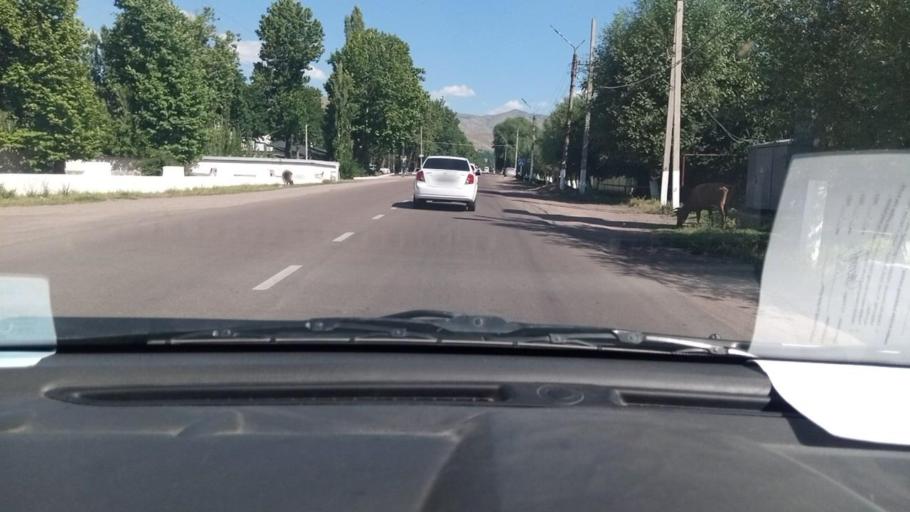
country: UZ
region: Toshkent
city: Angren
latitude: 41.0398
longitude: 70.0936
